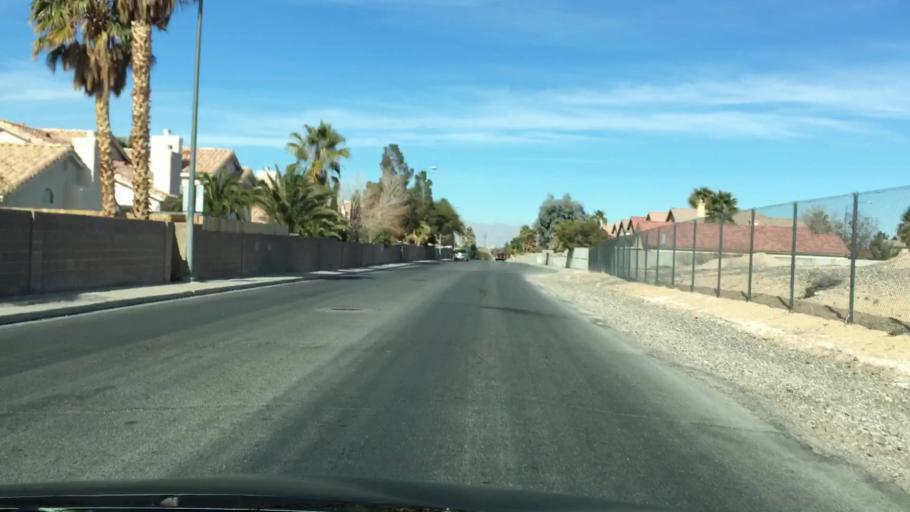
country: US
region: Nevada
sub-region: Clark County
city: Paradise
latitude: 36.0364
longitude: -115.1407
